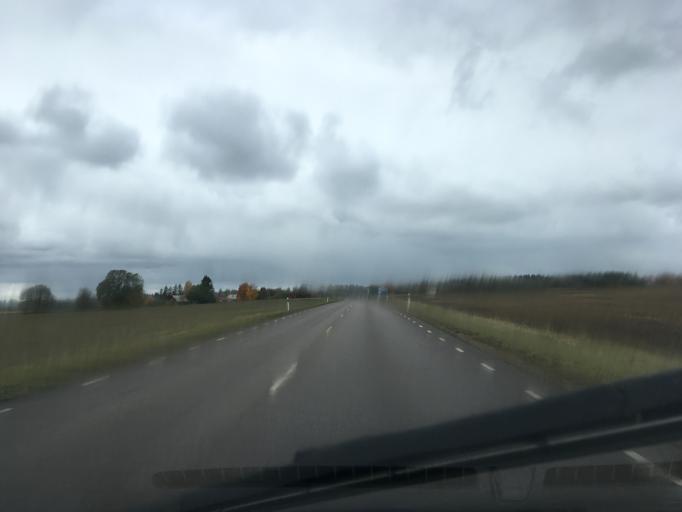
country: EE
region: Harju
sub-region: Anija vald
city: Kehra
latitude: 59.3274
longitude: 25.3256
